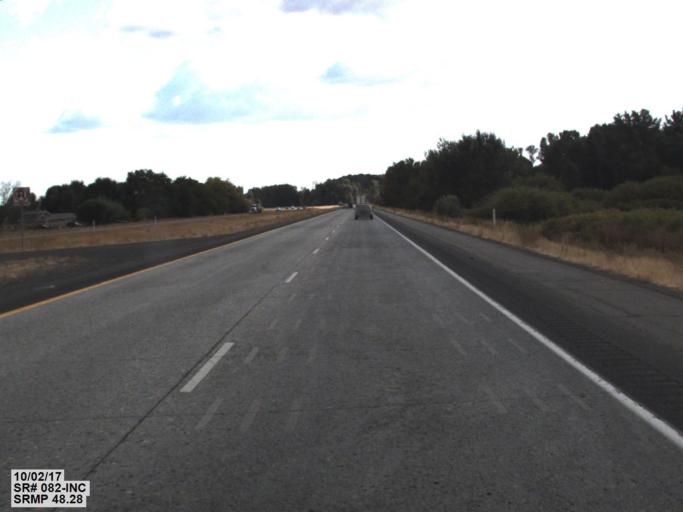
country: US
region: Washington
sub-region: Yakima County
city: Toppenish
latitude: 46.4306
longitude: -120.3434
